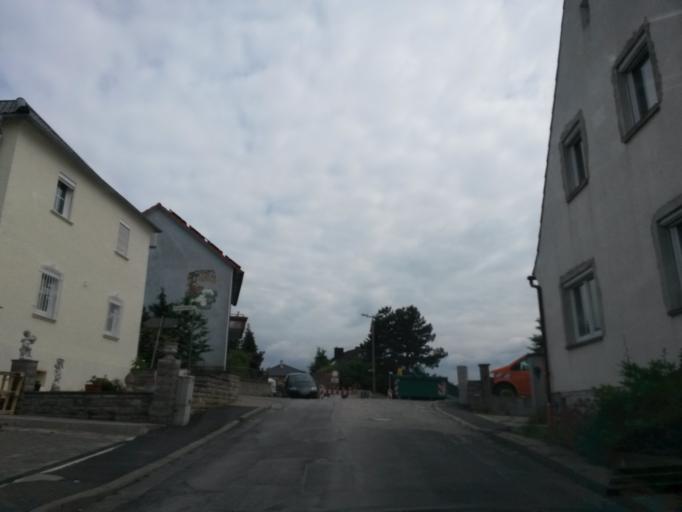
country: DE
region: Bavaria
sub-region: Regierungsbezirk Unterfranken
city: Rimpar
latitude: 49.8571
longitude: 9.9606
